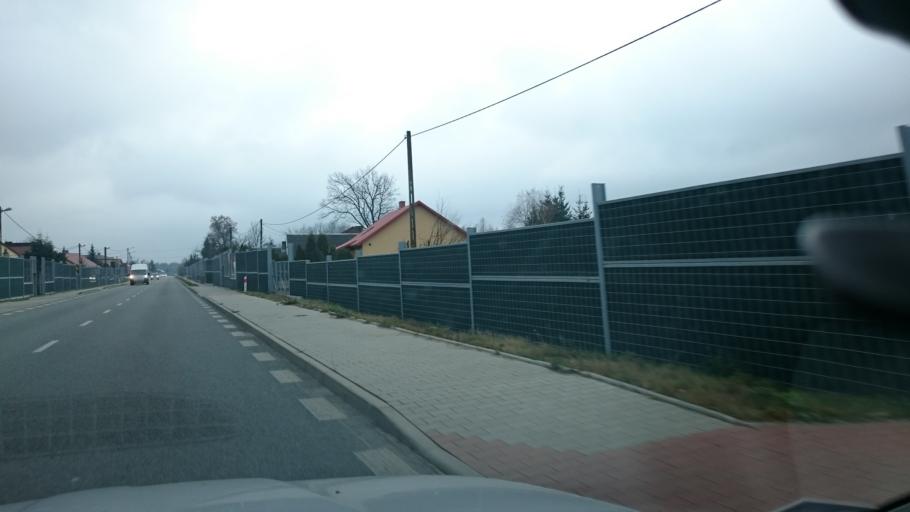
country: PL
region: Swietokrzyskie
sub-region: Powiat konecki
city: Konskie
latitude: 51.1473
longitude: 20.3623
